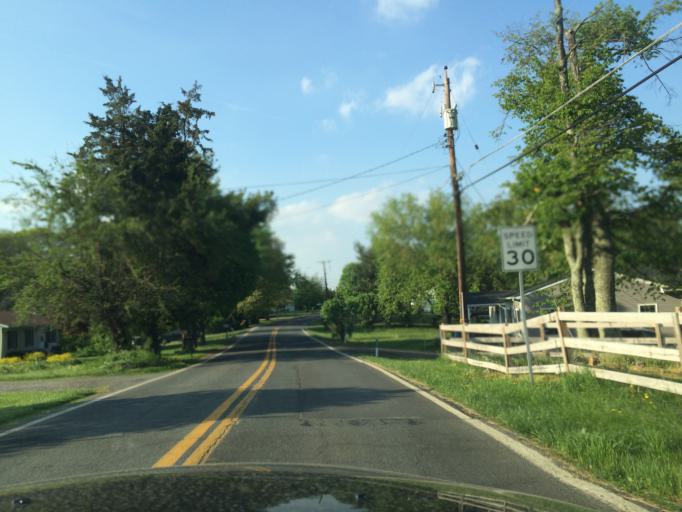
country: US
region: Maryland
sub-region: Carroll County
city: New Windsor
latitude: 39.4607
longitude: -77.0599
